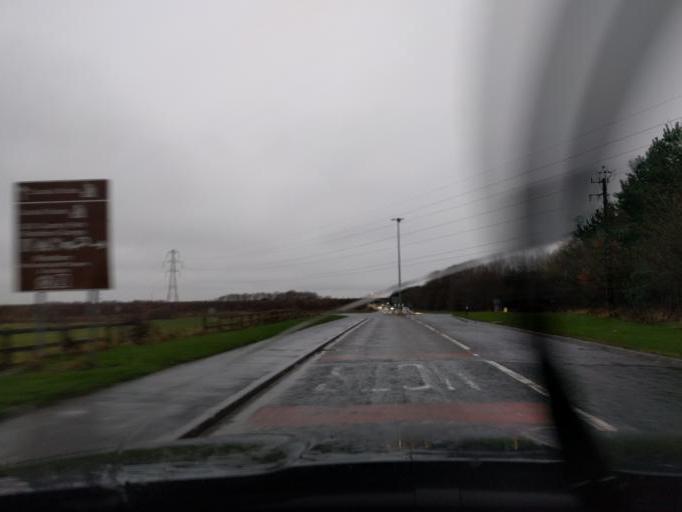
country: GB
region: England
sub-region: Northumberland
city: Newbiggin-by-the-Sea
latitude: 55.1914
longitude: -1.5363
